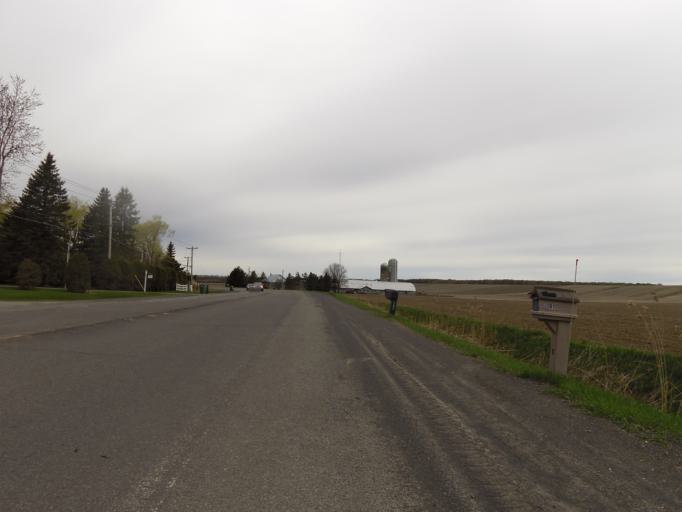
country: CA
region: Quebec
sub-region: Monteregie
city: Hudson
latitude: 45.5301
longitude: -74.1797
